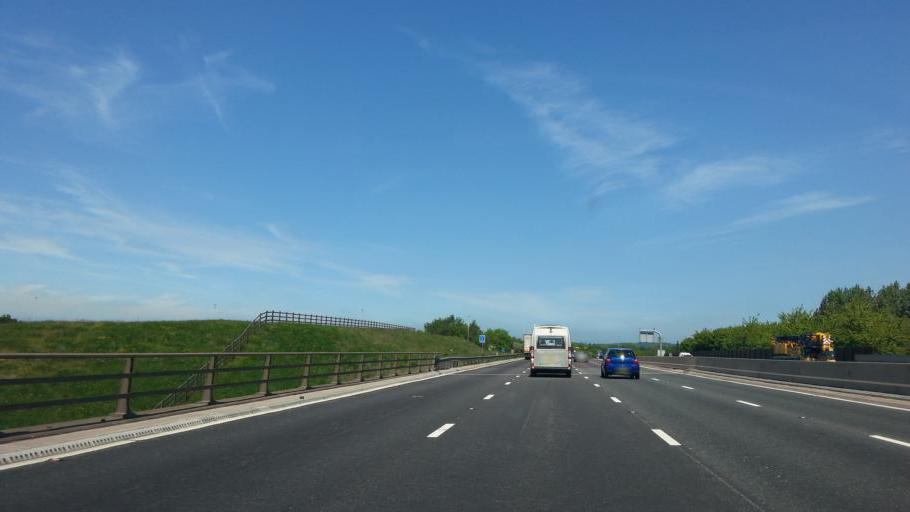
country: GB
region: England
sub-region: Worcestershire
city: Droitwich
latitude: 52.2874
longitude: -2.1203
